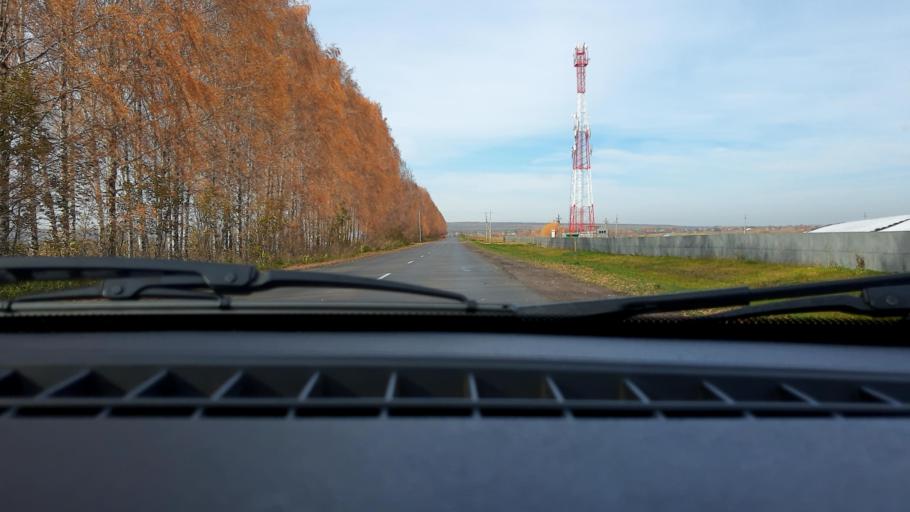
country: RU
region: Bashkortostan
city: Ufa
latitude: 54.8248
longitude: 55.9834
